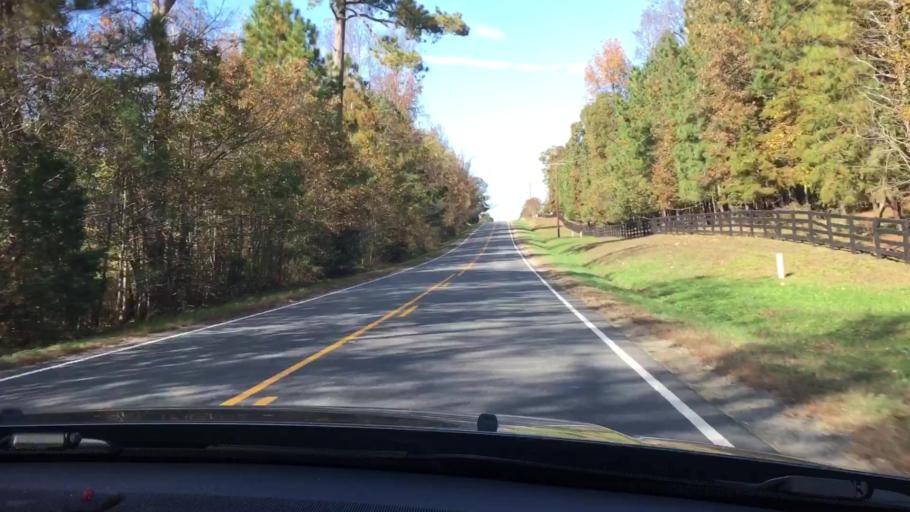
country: US
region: Virginia
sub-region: King and Queen County
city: King and Queen Court House
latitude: 37.6011
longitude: -76.9071
